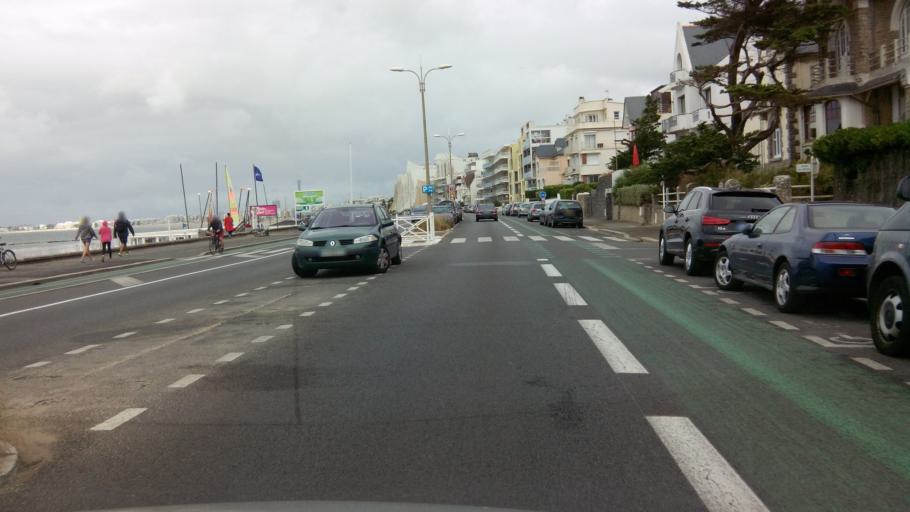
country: FR
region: Pays de la Loire
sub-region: Departement de la Loire-Atlantique
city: Pornichet
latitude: 47.2708
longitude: -2.3526
